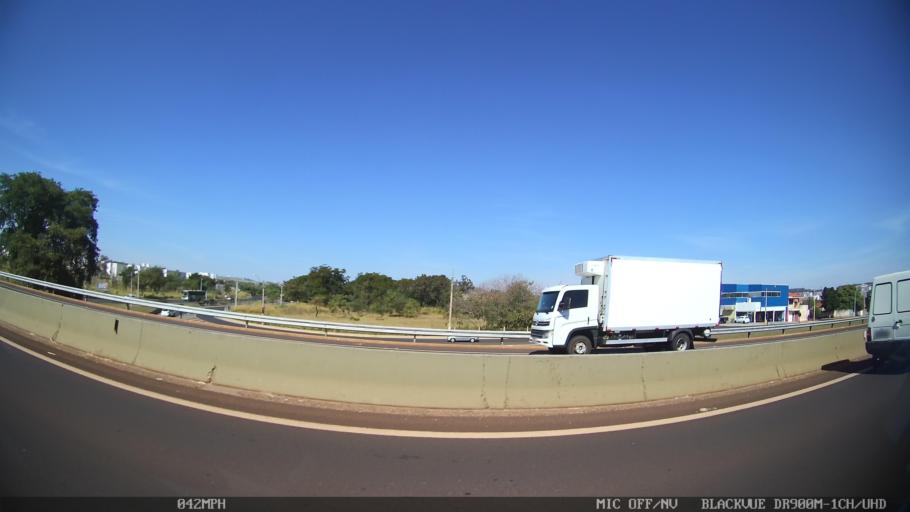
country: BR
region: Sao Paulo
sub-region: Ribeirao Preto
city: Ribeirao Preto
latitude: -21.2104
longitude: -47.7692
